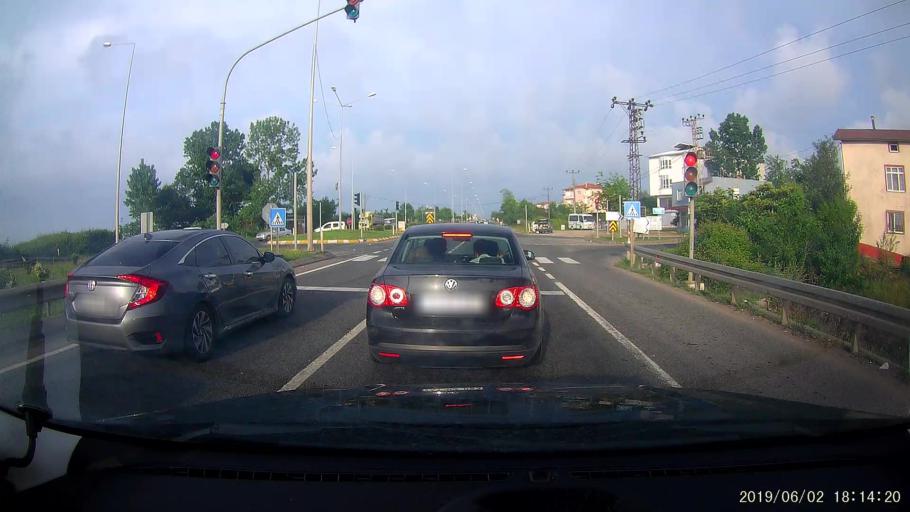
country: TR
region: Ordu
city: Unieh
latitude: 41.1065
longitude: 37.3695
